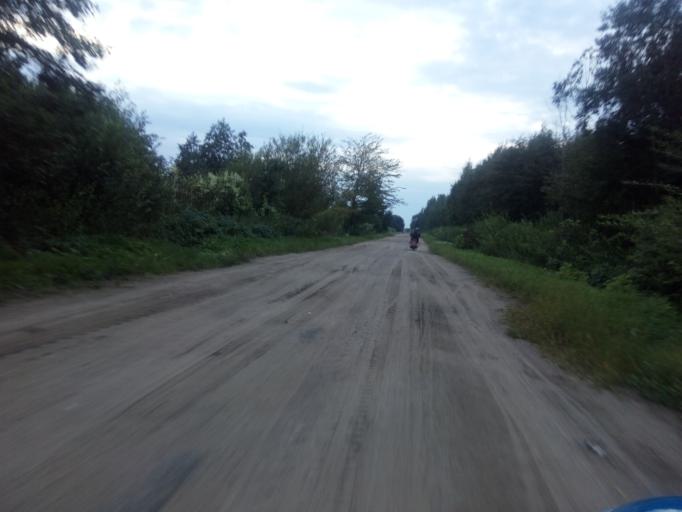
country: BY
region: Vitebsk
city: Dzisna
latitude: 55.6720
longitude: 28.3094
